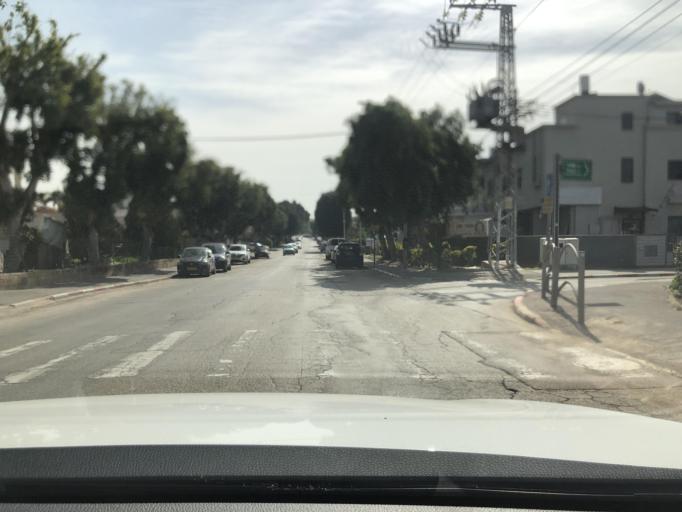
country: IL
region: Central District
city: Rosh Ha'Ayin
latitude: 32.0929
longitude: 34.9464
